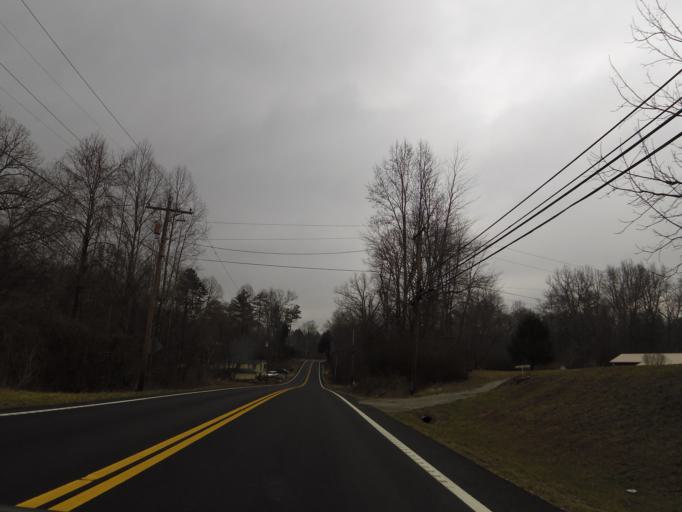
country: US
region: Tennessee
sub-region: Morgan County
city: Wartburg
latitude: 36.0775
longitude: -84.5467
